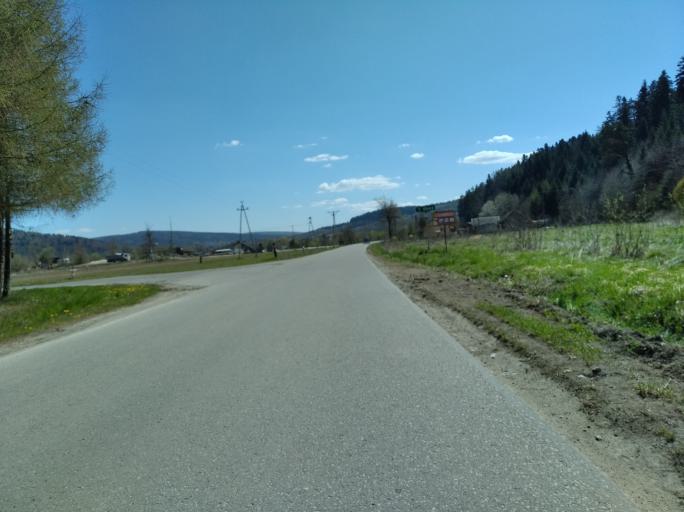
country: PL
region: Subcarpathian Voivodeship
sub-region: Powiat brzozowski
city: Dydnia
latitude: 49.6969
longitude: 22.1962
